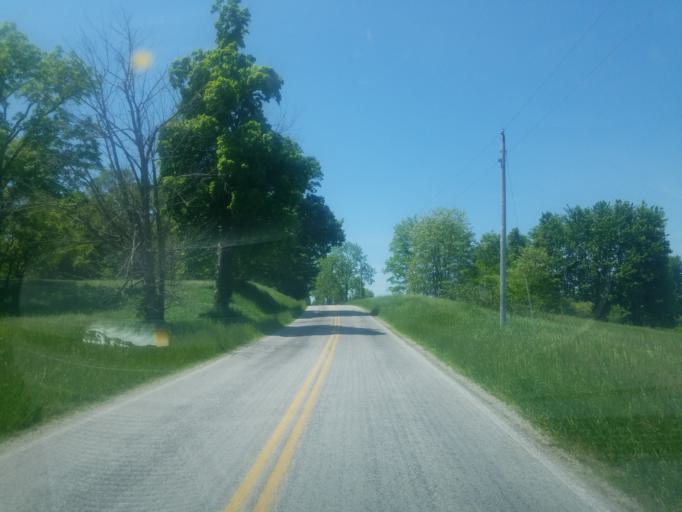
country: US
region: Ohio
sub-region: Huron County
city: New London
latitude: 41.1142
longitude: -82.4445
